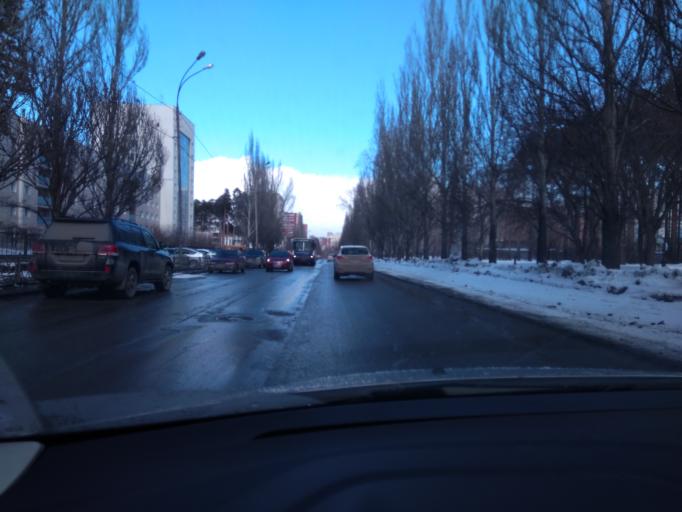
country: RU
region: Sverdlovsk
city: Sovkhoznyy
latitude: 56.8080
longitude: 60.5621
